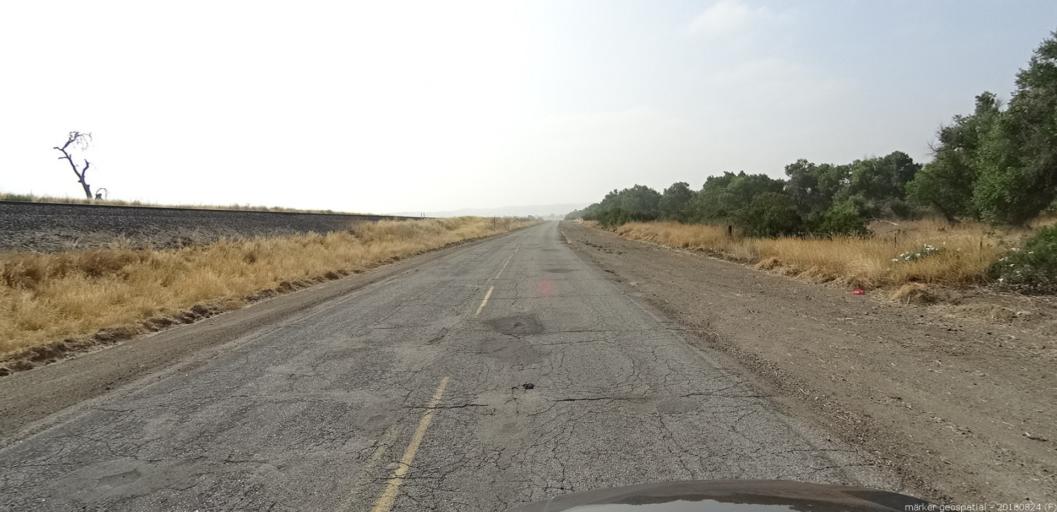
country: US
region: California
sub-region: San Luis Obispo County
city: San Miguel
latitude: 35.8588
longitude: -120.7649
